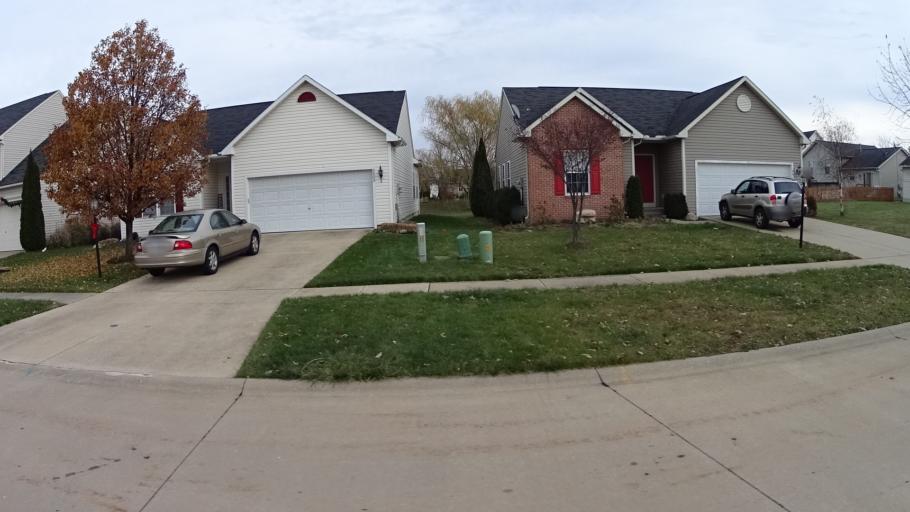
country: US
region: Ohio
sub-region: Lorain County
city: Sheffield
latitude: 41.4096
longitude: -82.0570
